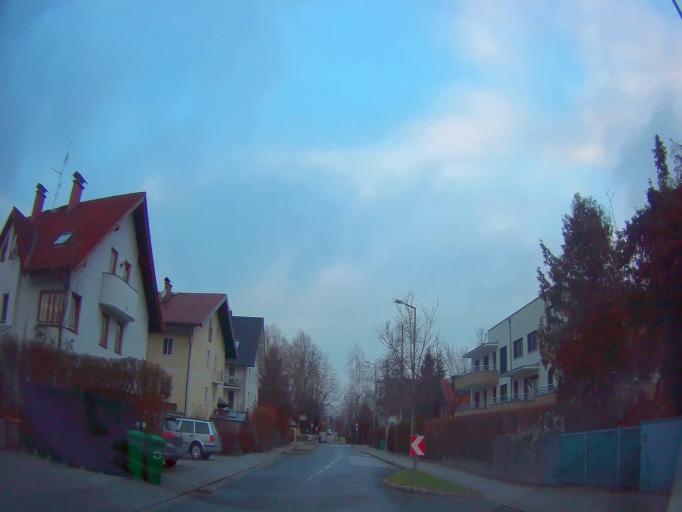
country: AT
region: Salzburg
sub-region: Salzburg Stadt
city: Salzburg
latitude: 47.8037
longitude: 13.0734
